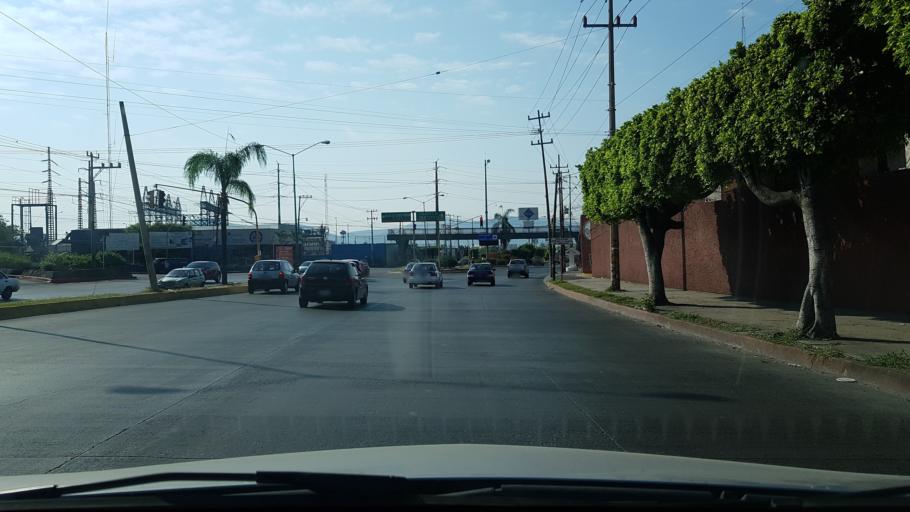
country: MX
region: Morelos
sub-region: Tepoztlan
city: Loma Bonita
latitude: 18.9116
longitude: -99.1817
